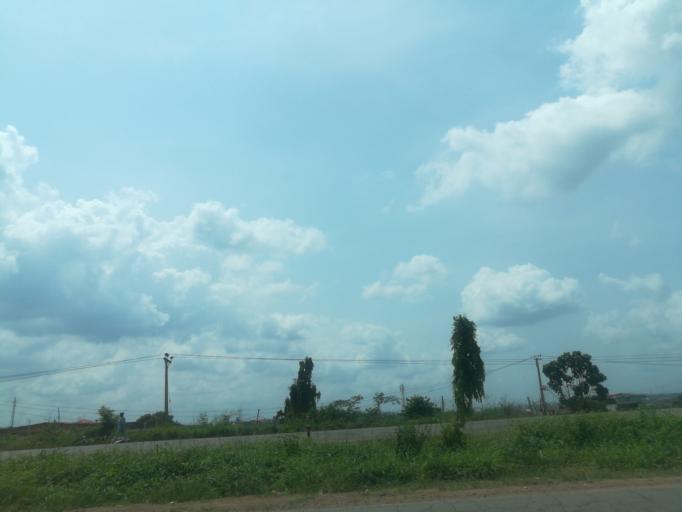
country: NG
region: Oyo
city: Ibadan
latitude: 7.4261
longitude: 3.9352
